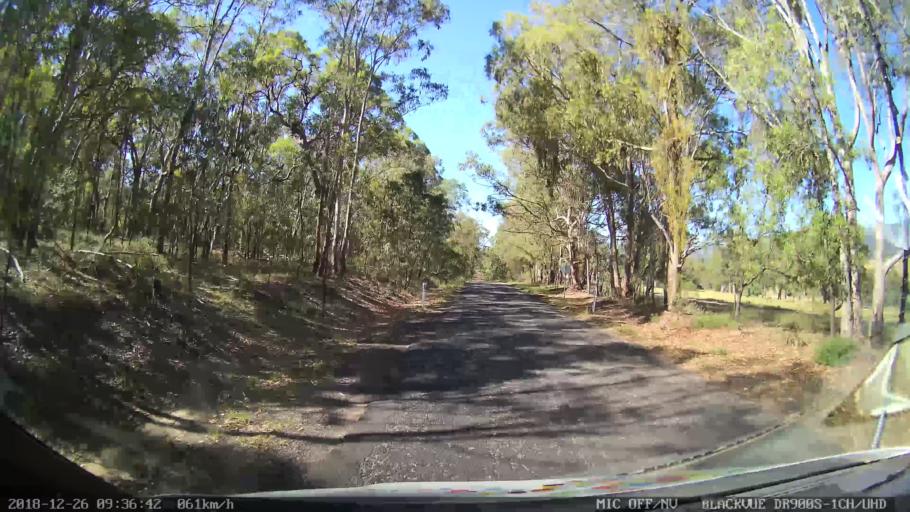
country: AU
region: New South Wales
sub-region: Mid-Western Regional
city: Kandos
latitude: -32.9261
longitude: 150.0398
